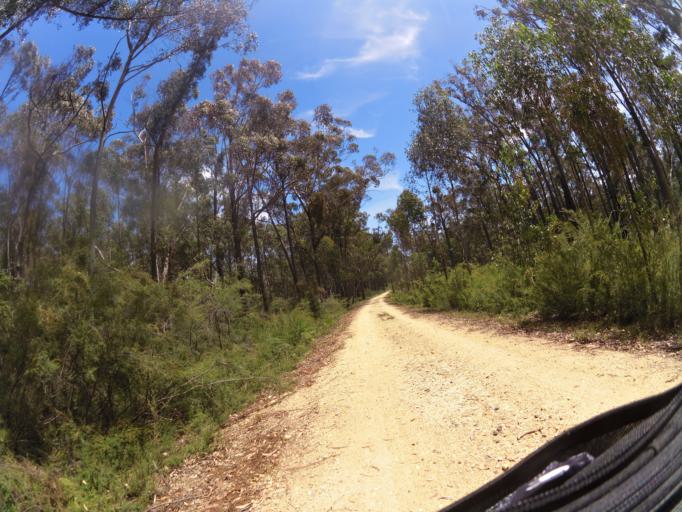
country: AU
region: Victoria
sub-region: East Gippsland
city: Lakes Entrance
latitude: -37.7591
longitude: 147.9536
